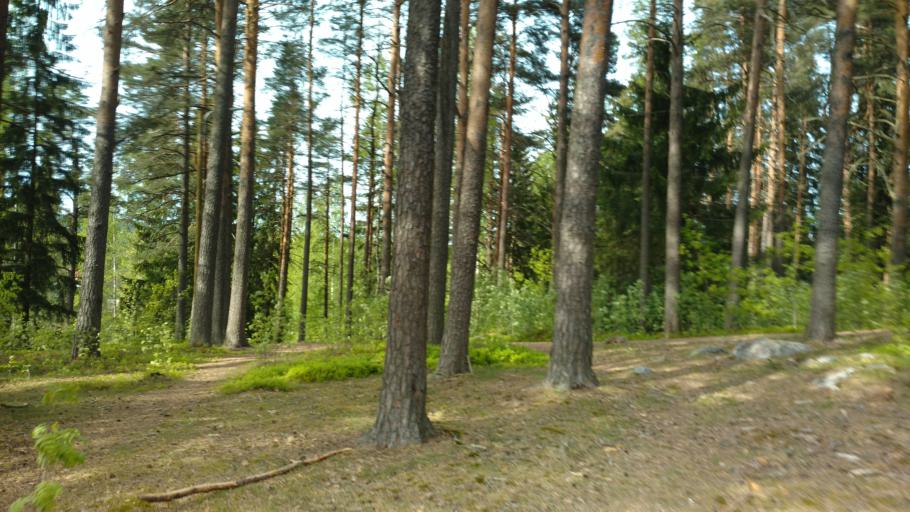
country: FI
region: Varsinais-Suomi
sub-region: Salo
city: Salo
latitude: 60.3848
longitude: 23.1500
